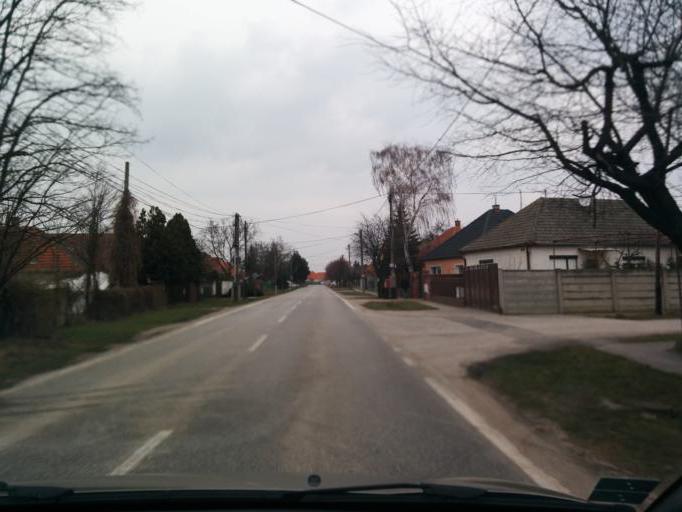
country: SK
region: Trnavsky
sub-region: Okres Galanta
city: Galanta
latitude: 48.2606
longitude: 17.8063
